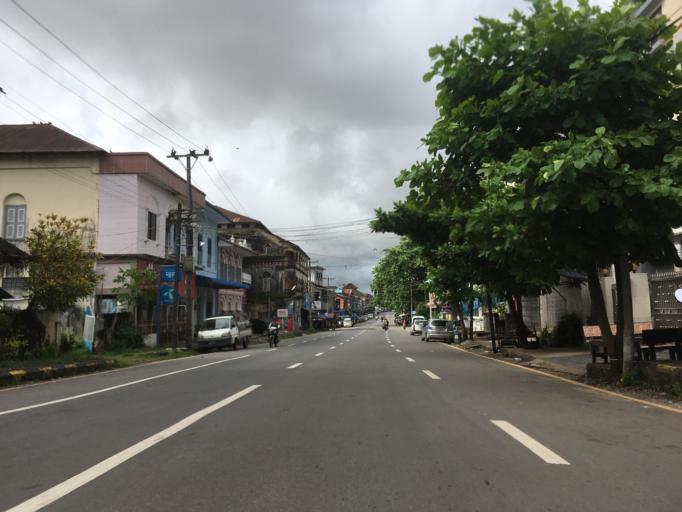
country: MM
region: Mon
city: Mawlamyine
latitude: 16.4706
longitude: 97.6224
